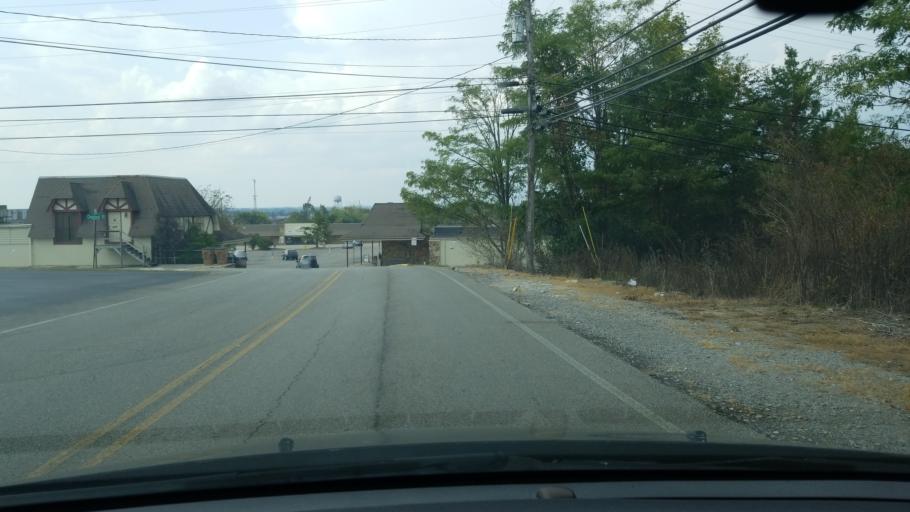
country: US
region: Tennessee
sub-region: Cumberland County
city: Crossville
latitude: 35.9563
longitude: -85.0294
